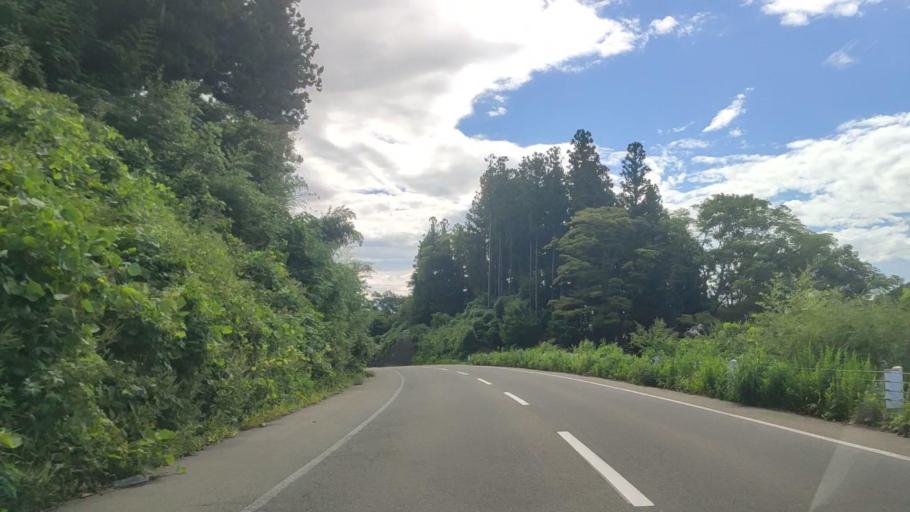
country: JP
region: Nagano
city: Nakano
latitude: 36.7813
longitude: 138.3202
